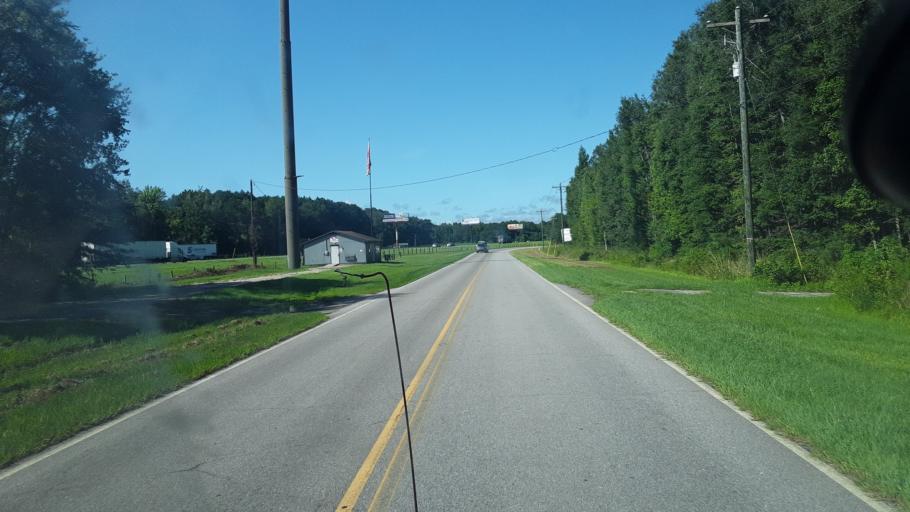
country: US
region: South Carolina
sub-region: Hampton County
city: Yemassee
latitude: 32.5988
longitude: -80.9068
